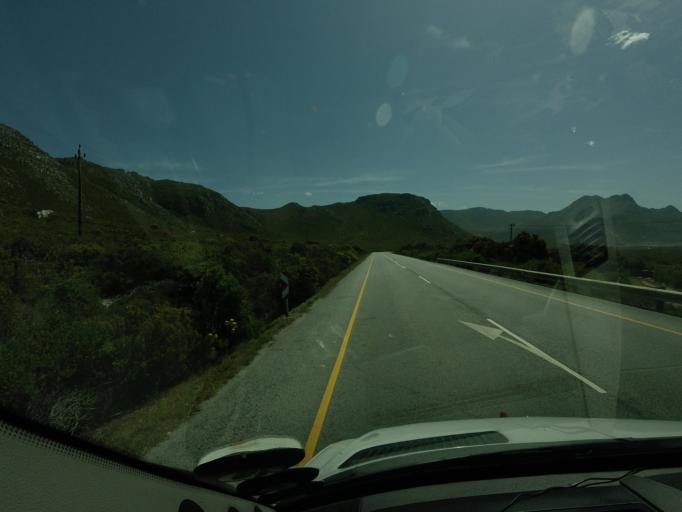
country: ZA
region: Western Cape
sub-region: Overberg District Municipality
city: Grabouw
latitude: -34.3498
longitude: 18.9750
